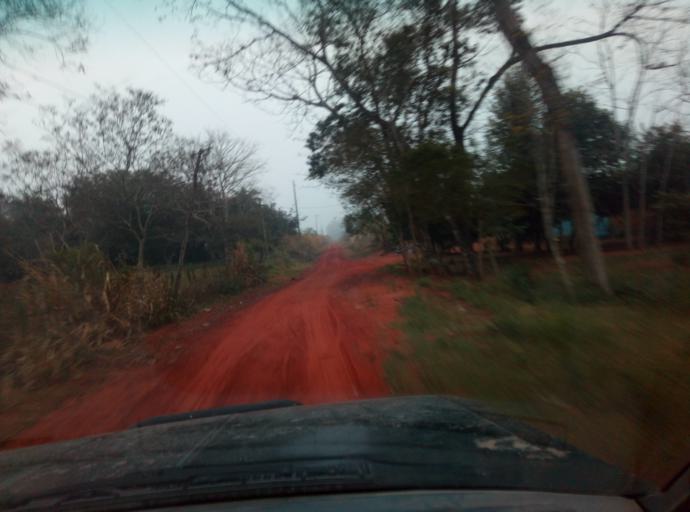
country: PY
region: Caaguazu
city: Doctor Cecilio Baez
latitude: -25.1592
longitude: -56.2628
